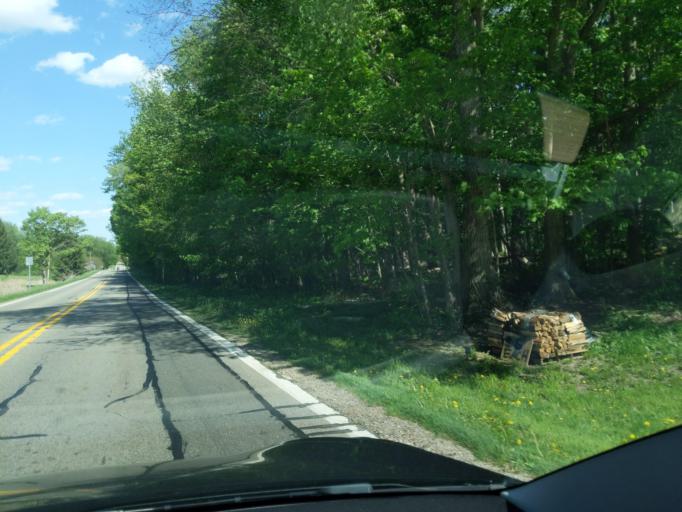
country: US
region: Michigan
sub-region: Kent County
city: Lowell
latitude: 42.7985
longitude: -85.3412
